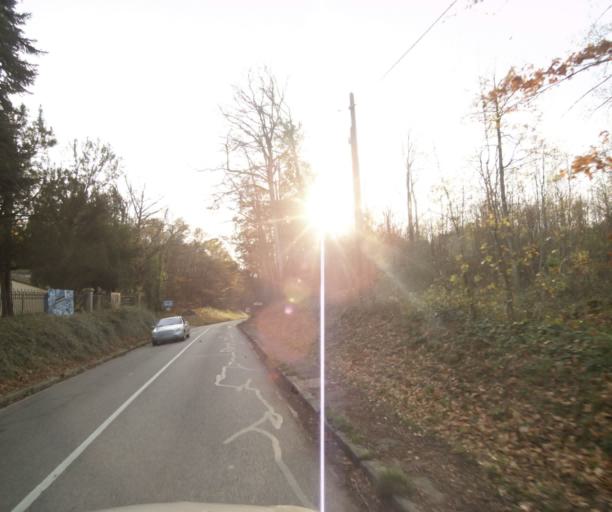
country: FR
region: Ile-de-France
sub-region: Departement des Yvelines
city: Triel-sur-Seine
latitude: 48.9986
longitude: 2.0090
